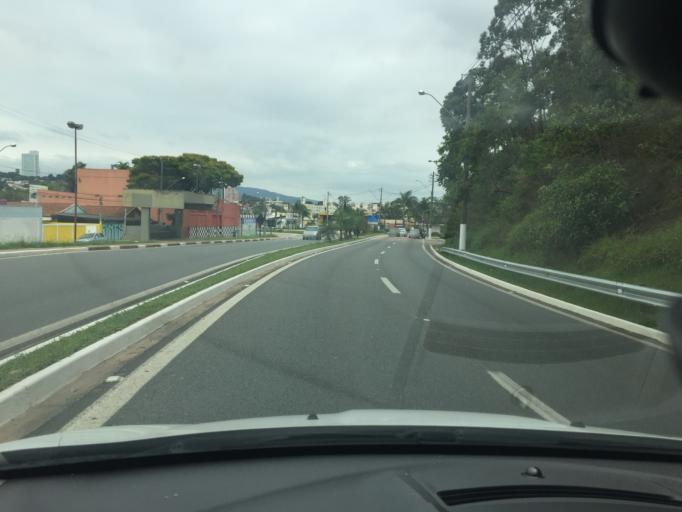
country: BR
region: Sao Paulo
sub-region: Jundiai
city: Jundiai
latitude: -23.1709
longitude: -46.8836
